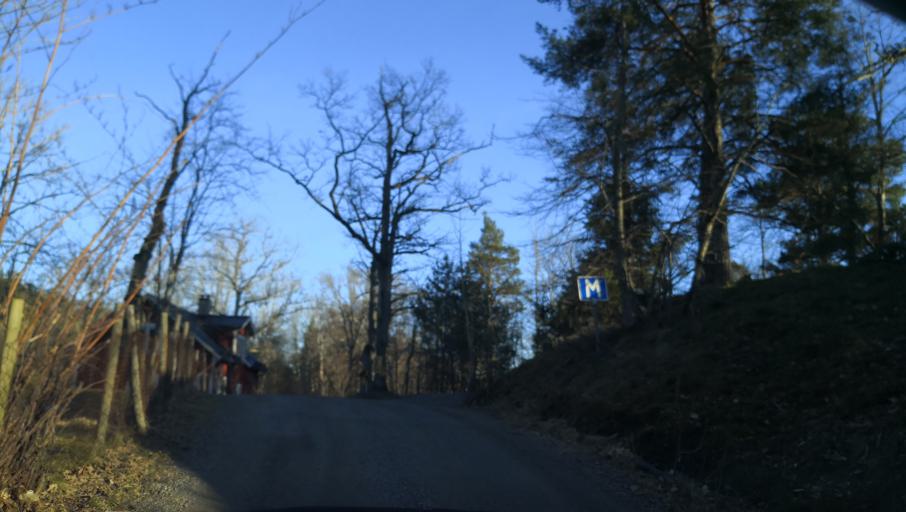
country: SE
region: Stockholm
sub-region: Varmdo Kommun
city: Mortnas
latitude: 59.3319
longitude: 18.4333
